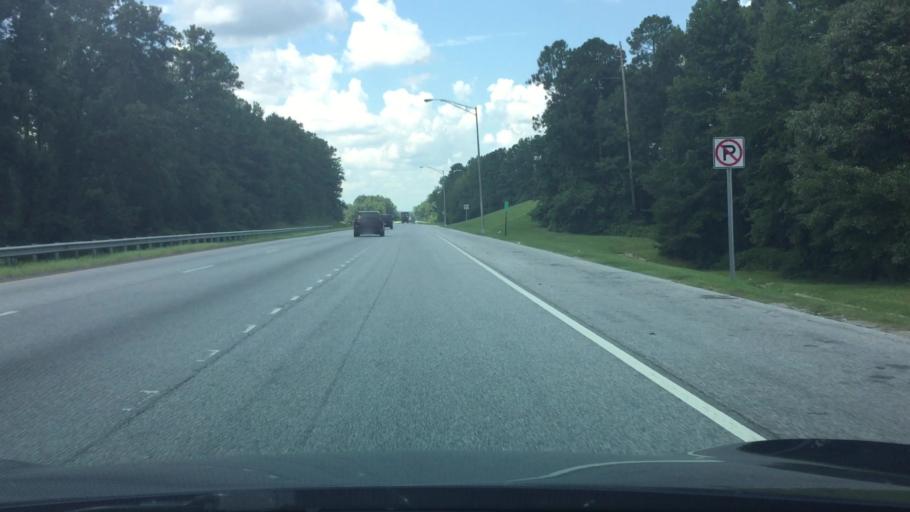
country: US
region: Alabama
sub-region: Macon County
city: Tuskegee
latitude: 32.5017
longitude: -85.6125
